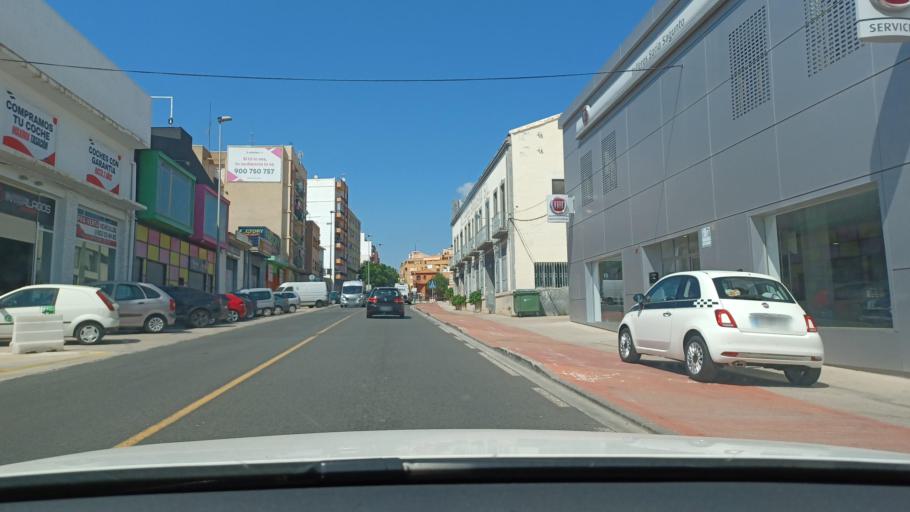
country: ES
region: Valencia
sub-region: Provincia de Valencia
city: Sagunto
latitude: 39.6733
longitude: -0.2750
